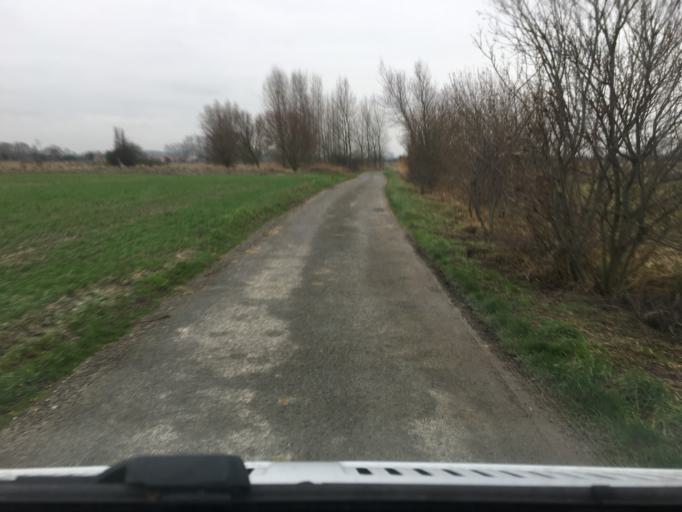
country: FR
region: Picardie
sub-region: Departement de la Somme
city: Pende
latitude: 50.1779
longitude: 1.5433
